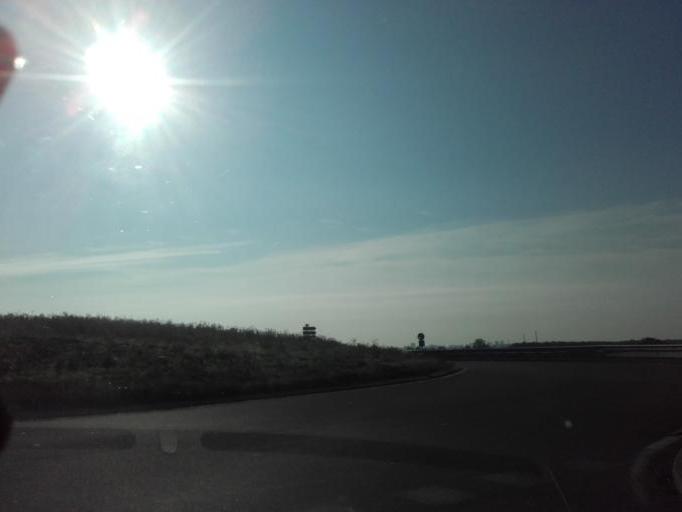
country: FR
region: Bourgogne
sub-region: Departement de Saone-et-Loire
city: Champforgeuil
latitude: 46.8267
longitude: 4.8290
